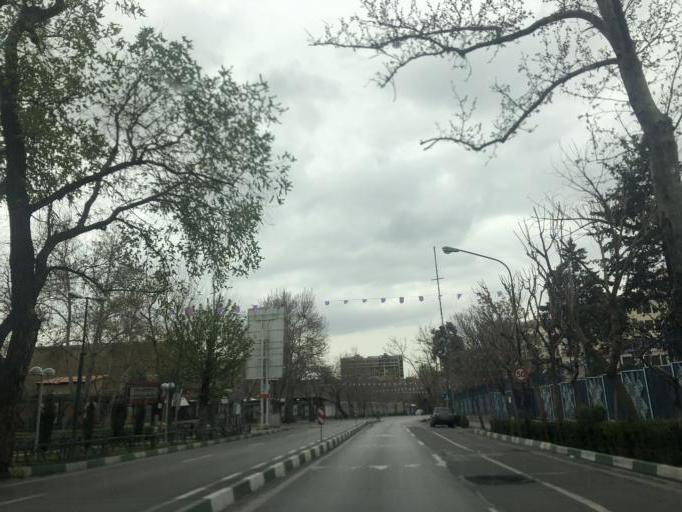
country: IR
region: Tehran
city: Tajrish
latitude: 35.7789
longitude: 51.4670
